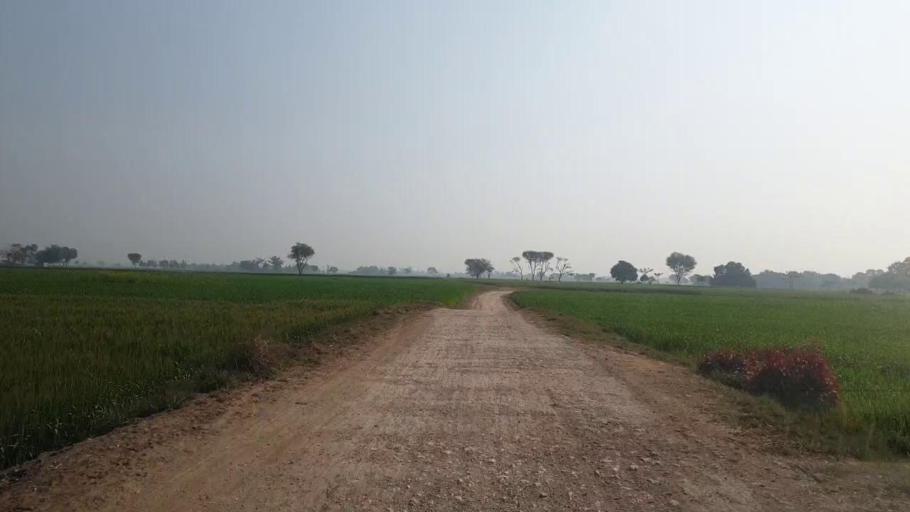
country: PK
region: Sindh
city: Bhit Shah
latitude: 25.7316
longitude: 68.5219
